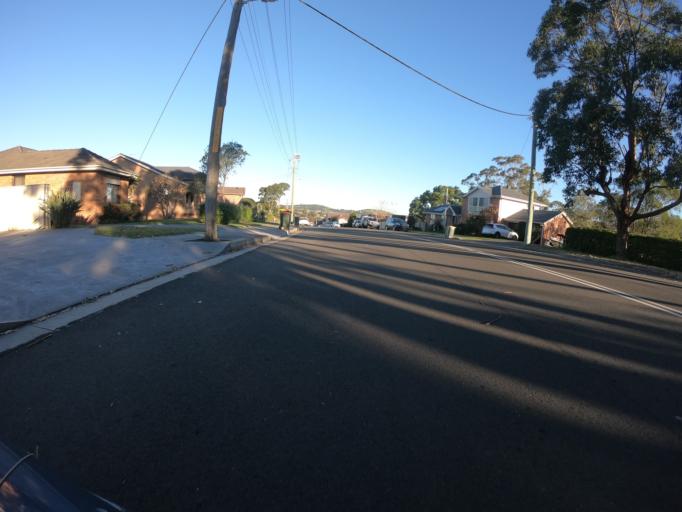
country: AU
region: New South Wales
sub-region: Wollongong
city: Cordeaux Heights
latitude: -34.4303
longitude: 150.8431
